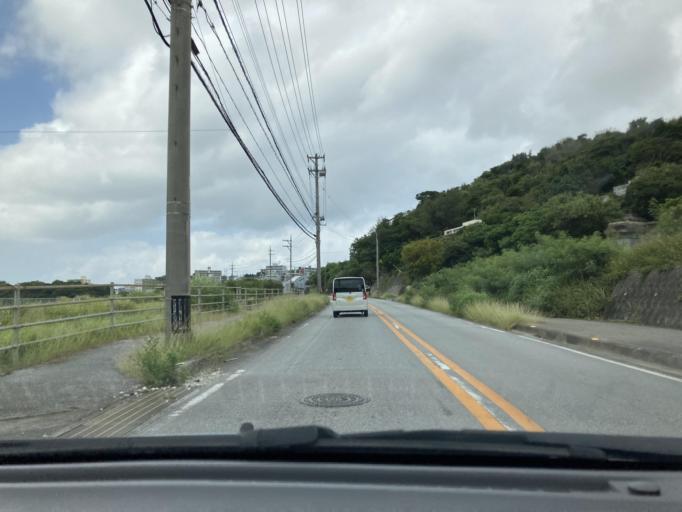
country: JP
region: Okinawa
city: Ginowan
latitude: 26.2403
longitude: 127.7567
